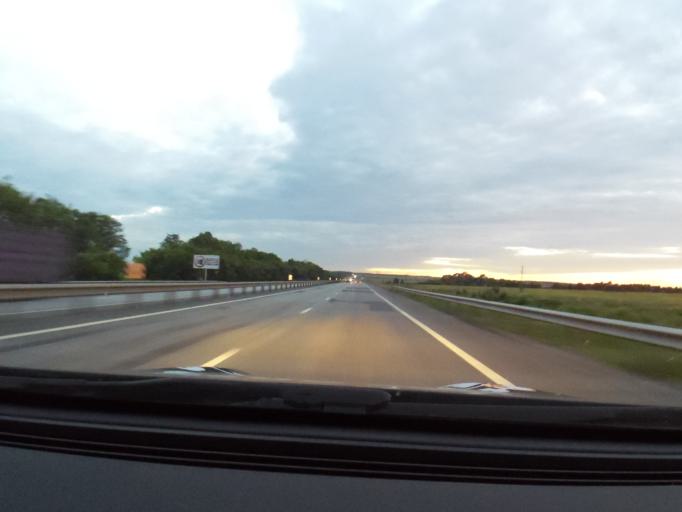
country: RU
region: Chuvashia
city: Yadrin
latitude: 55.9975
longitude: 46.1197
